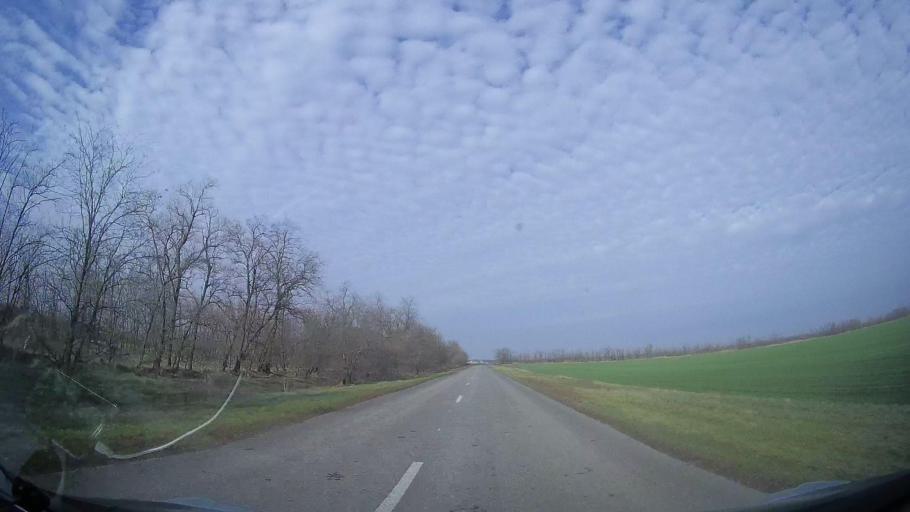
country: RU
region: Rostov
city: Gigant
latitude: 46.8744
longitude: 41.2729
